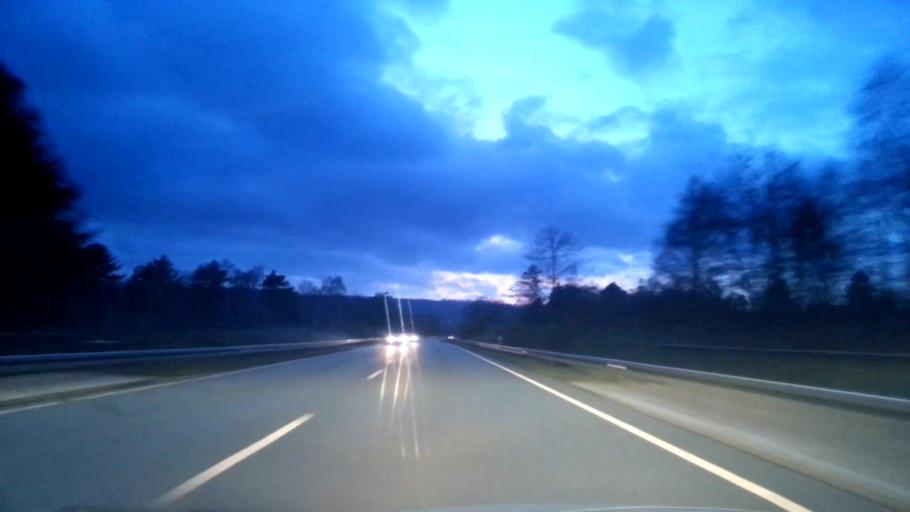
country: DE
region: Bavaria
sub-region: Upper Franconia
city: Seybothenreuth
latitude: 49.9448
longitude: 11.7307
